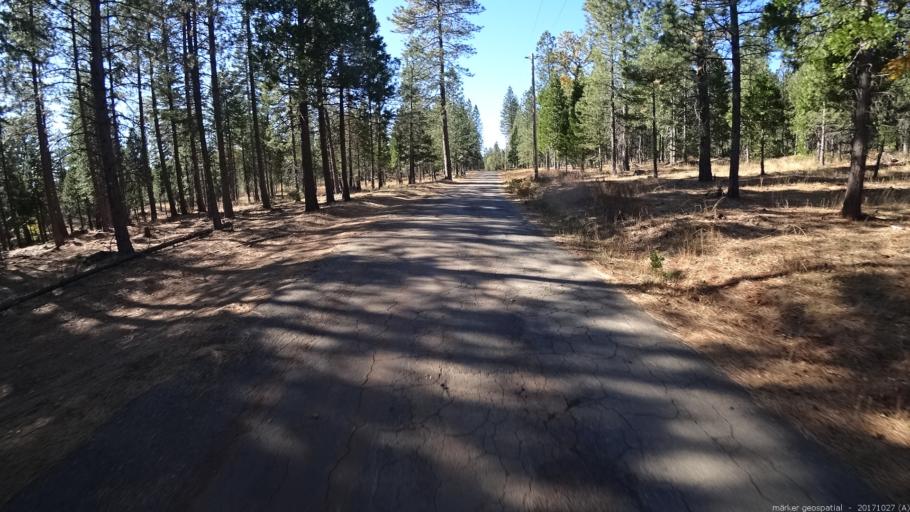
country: US
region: California
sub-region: Shasta County
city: Shingletown
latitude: 40.6136
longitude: -121.8220
